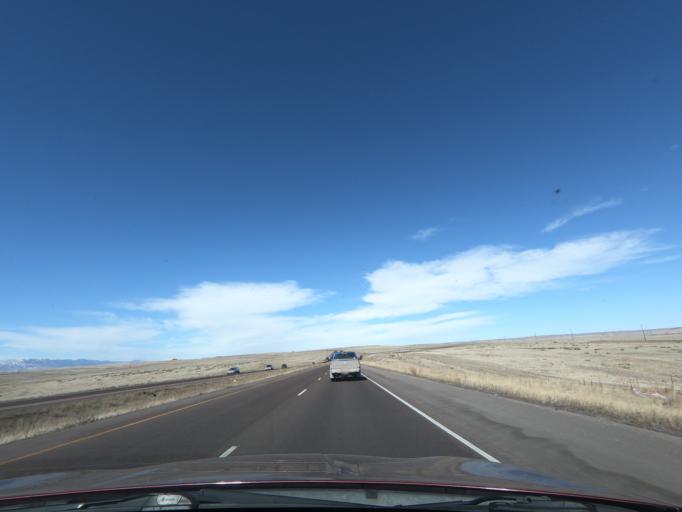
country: US
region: Colorado
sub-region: El Paso County
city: Security-Widefield
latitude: 38.7472
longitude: -104.6827
